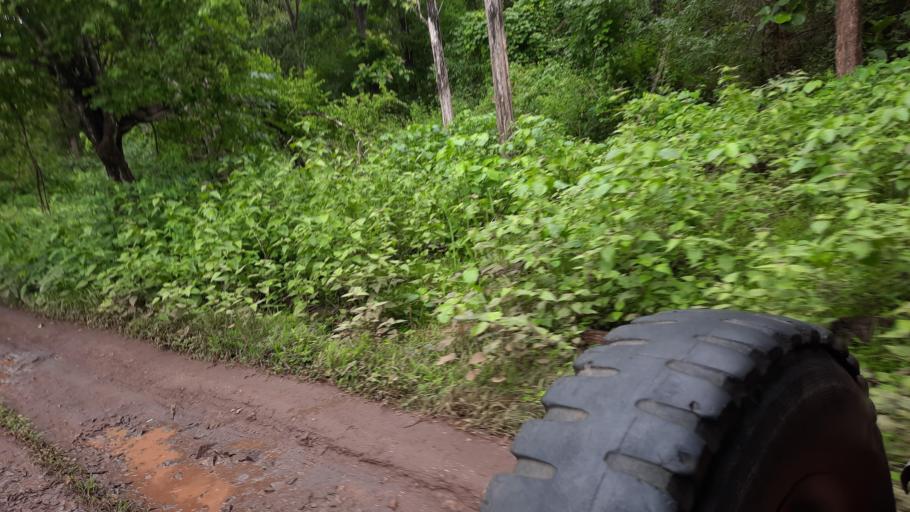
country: IN
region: Kerala
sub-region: Wayanad
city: Panamaram
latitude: 11.9358
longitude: 76.0858
